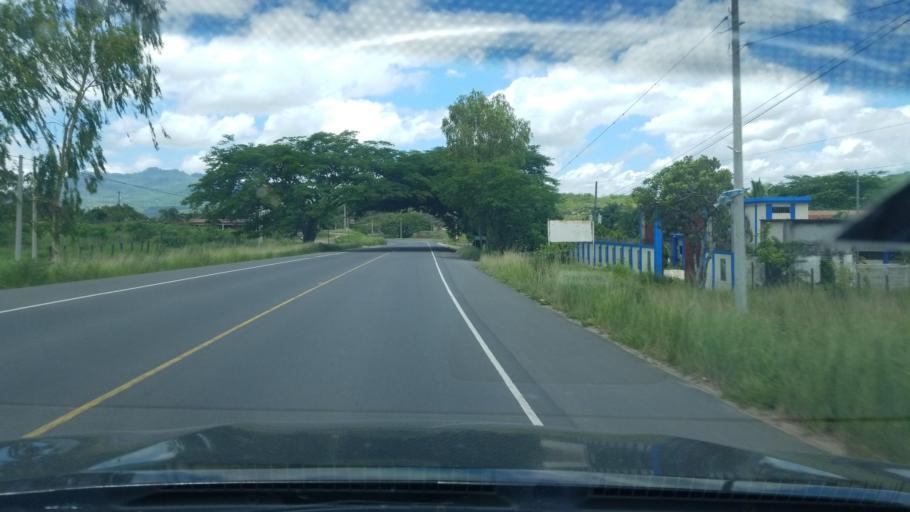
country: HN
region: Francisco Morazan
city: Cofradia
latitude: 14.2856
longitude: -87.2432
